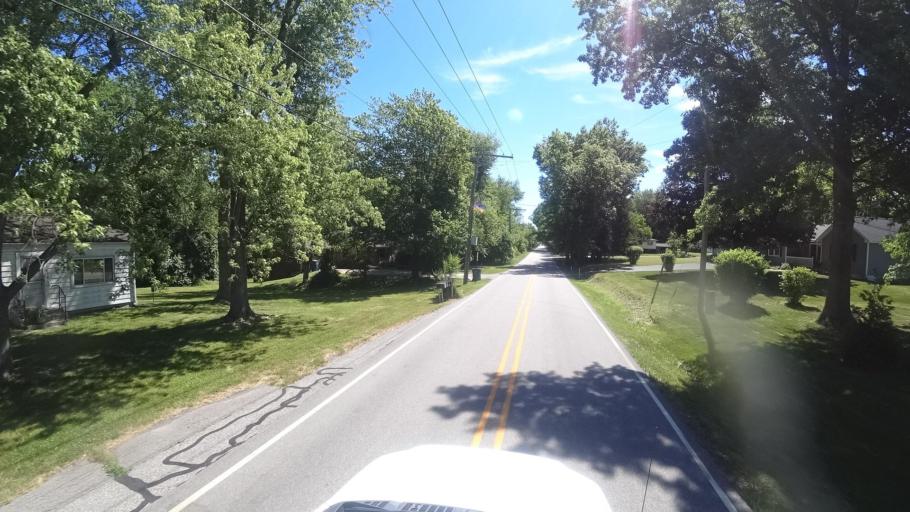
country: US
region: Indiana
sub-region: Porter County
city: Chesterton
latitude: 41.6296
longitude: -87.0598
